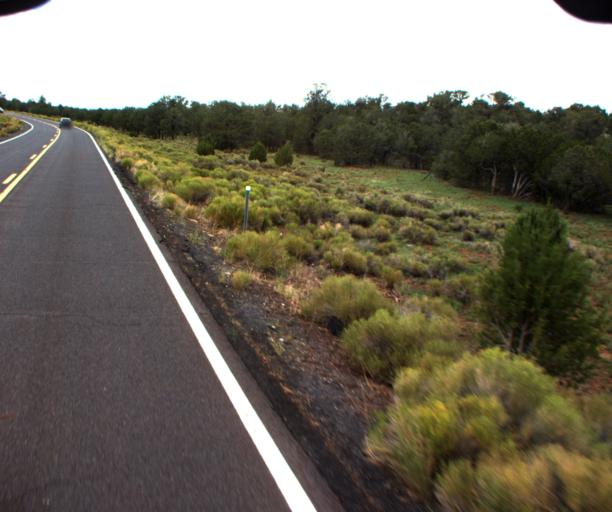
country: US
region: Arizona
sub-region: Coconino County
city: Parks
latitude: 35.5406
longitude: -111.8536
